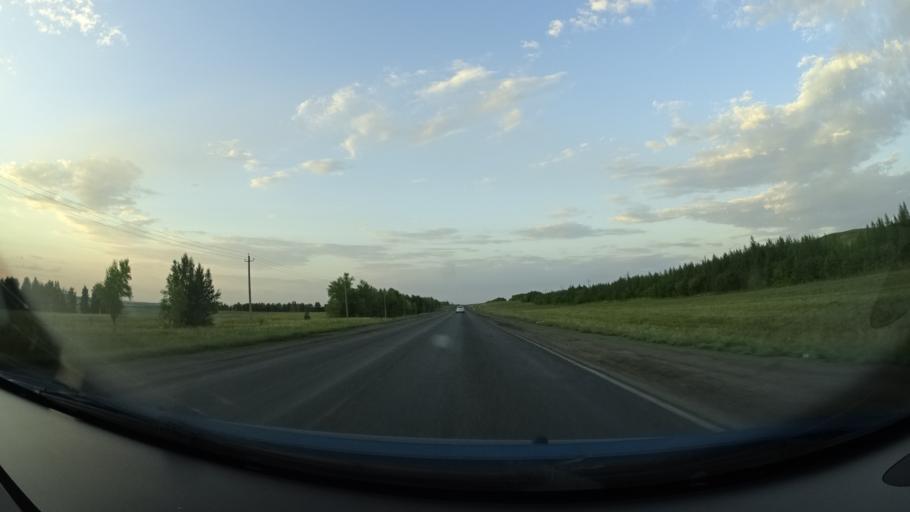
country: RU
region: Orenburg
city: Severnoye
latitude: 54.1930
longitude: 52.6775
